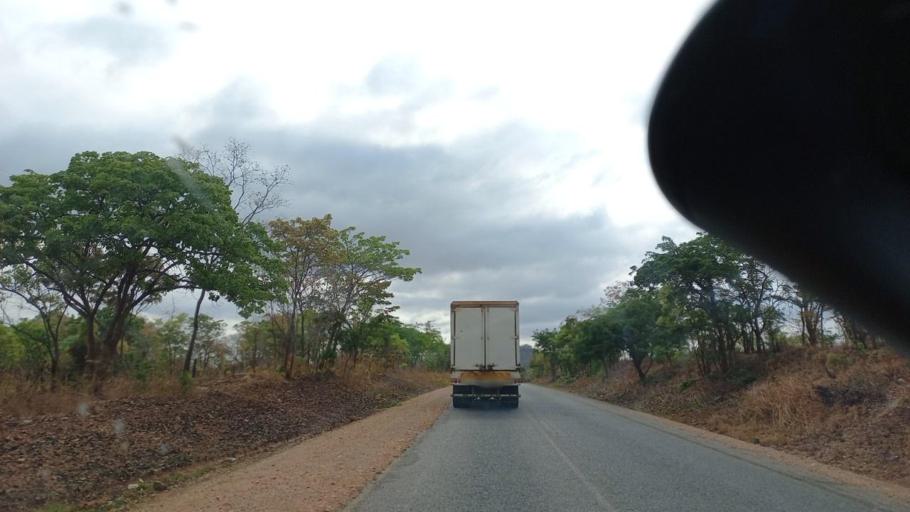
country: ZM
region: Lusaka
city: Chongwe
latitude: -15.1314
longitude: 29.5122
